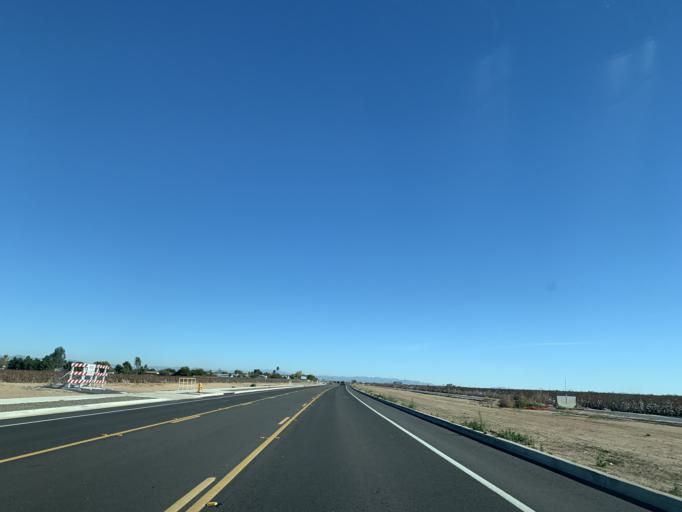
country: US
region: Arizona
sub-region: Maricopa County
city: Queen Creek
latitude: 33.2195
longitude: -111.6141
